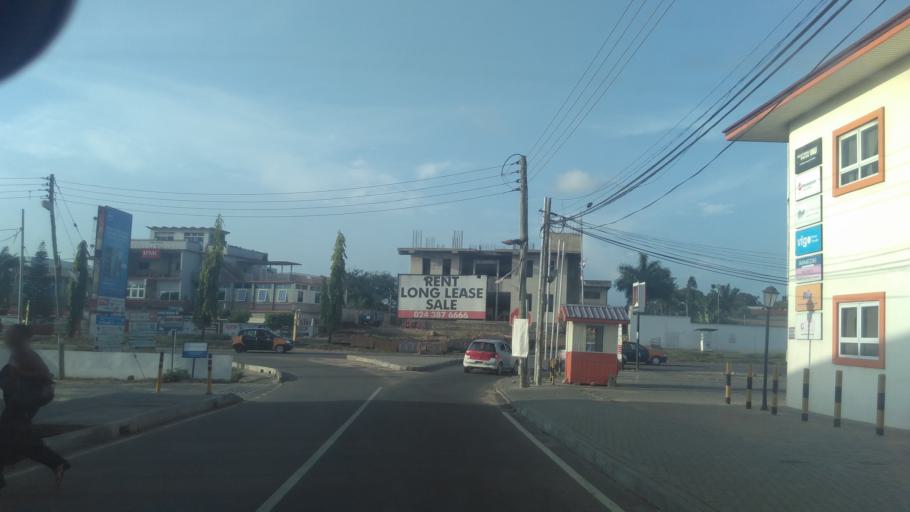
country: GH
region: Greater Accra
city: Accra
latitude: 5.5720
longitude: -0.2034
